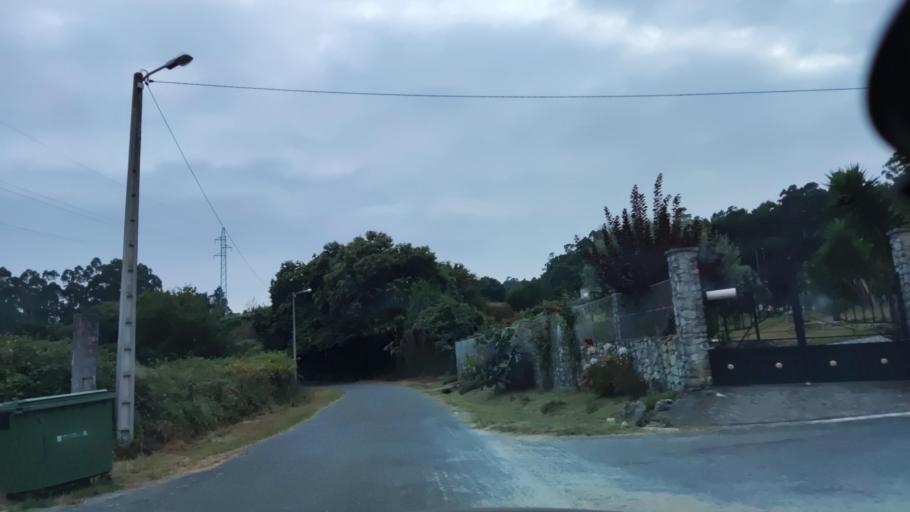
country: ES
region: Galicia
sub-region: Provincia de Pontevedra
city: Catoira
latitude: 42.7092
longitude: -8.7220
